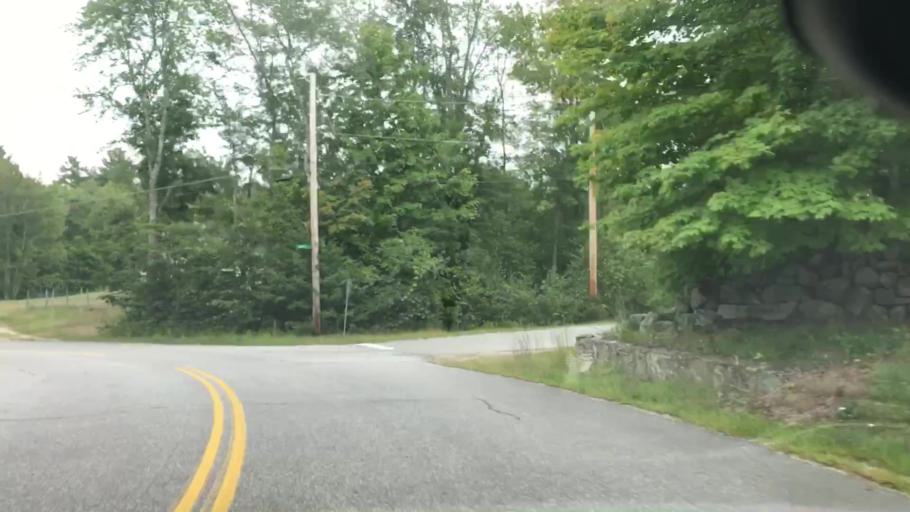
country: US
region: New Hampshire
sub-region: Hillsborough County
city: Milford
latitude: 42.8506
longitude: -71.5728
